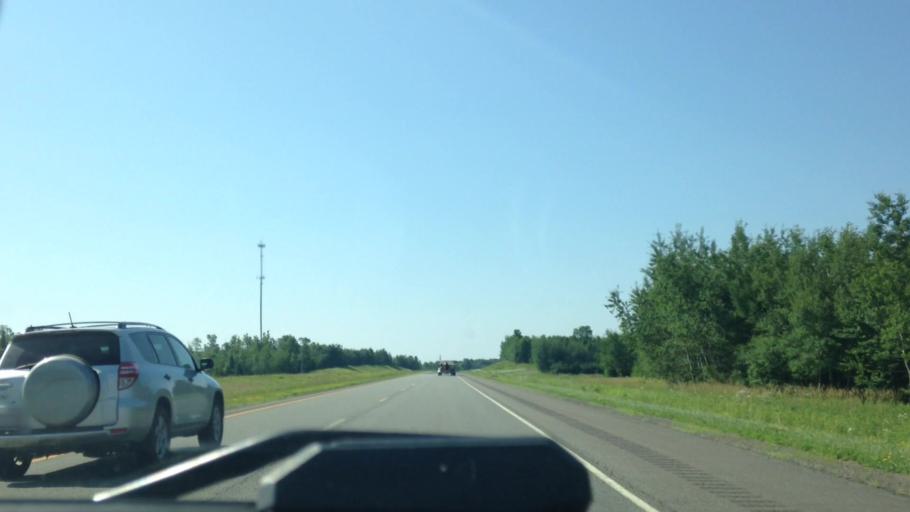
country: US
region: Wisconsin
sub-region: Douglas County
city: Lake Nebagamon
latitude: 46.4286
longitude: -91.8118
